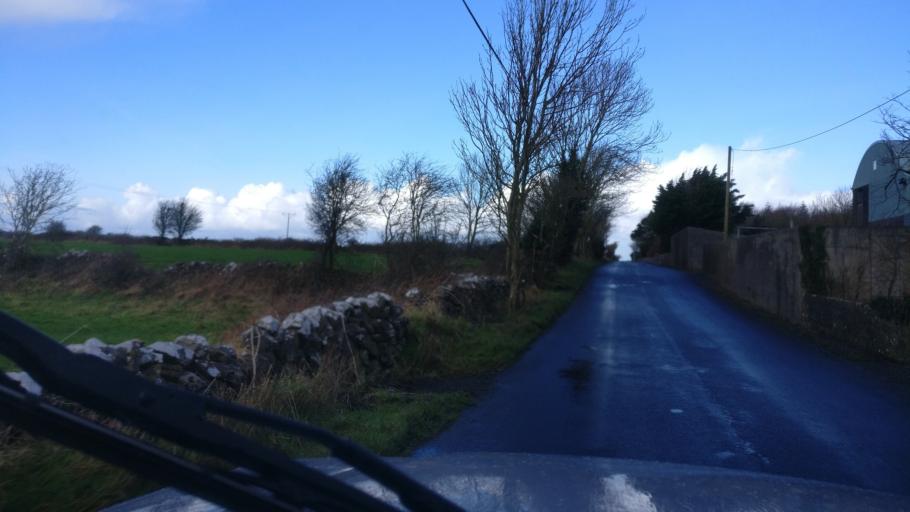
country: IE
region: Connaught
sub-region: County Galway
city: Oranmore
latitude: 53.2607
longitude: -8.8626
